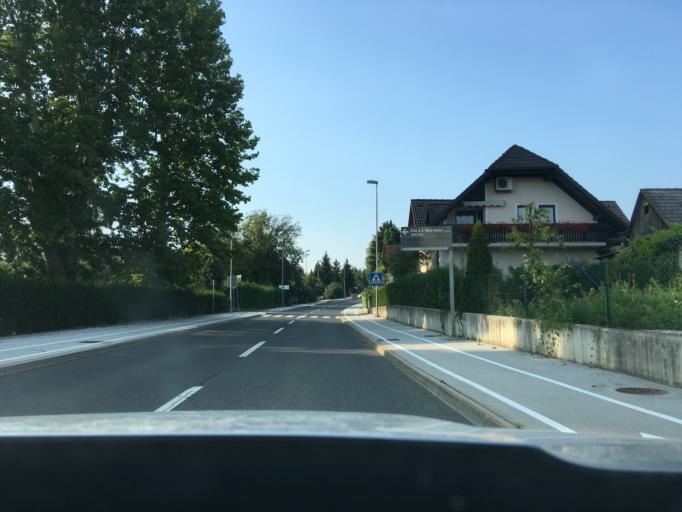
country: SI
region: Novo Mesto
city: Novo Mesto
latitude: 45.7891
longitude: 15.1792
